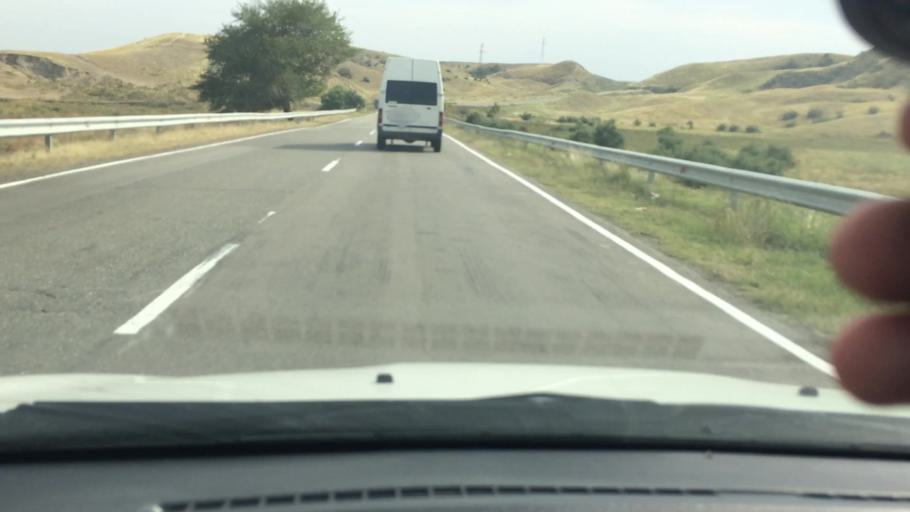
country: GE
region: Kvemo Kartli
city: Rust'avi
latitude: 41.5295
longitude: 44.9858
